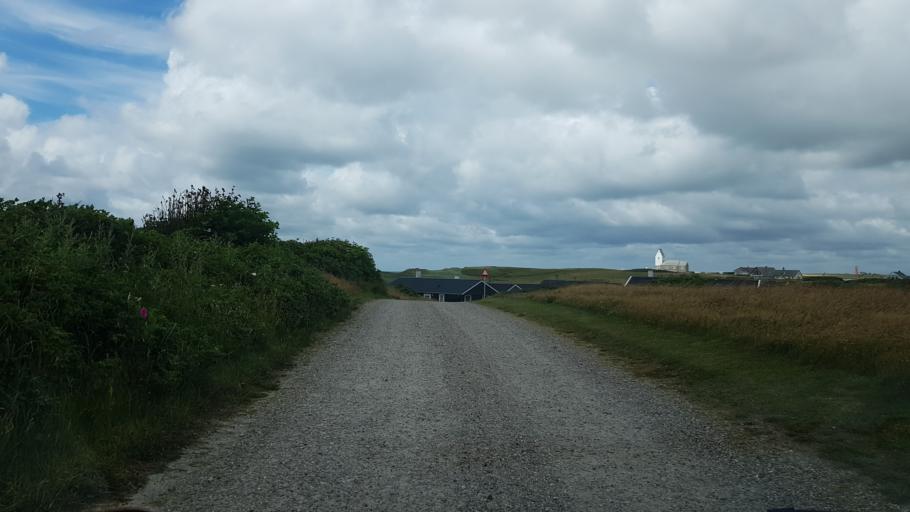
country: DK
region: Central Jutland
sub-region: Lemvig Kommune
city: Harboore
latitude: 56.4922
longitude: 8.1259
